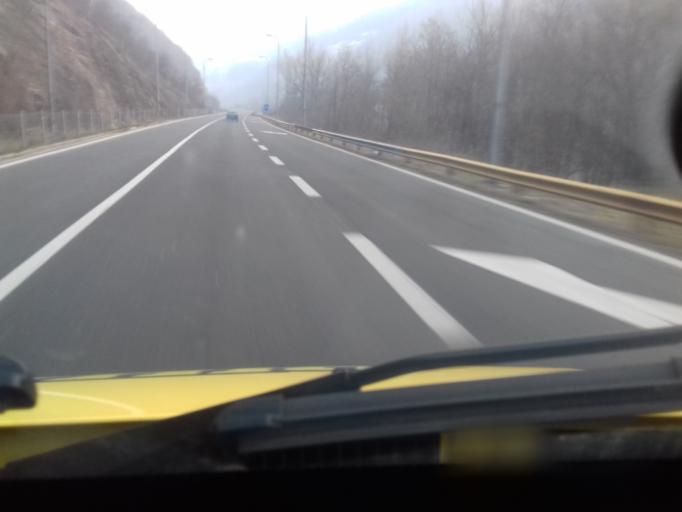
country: BA
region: Federation of Bosnia and Herzegovina
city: Busovaca
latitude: 44.1378
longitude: 17.9336
